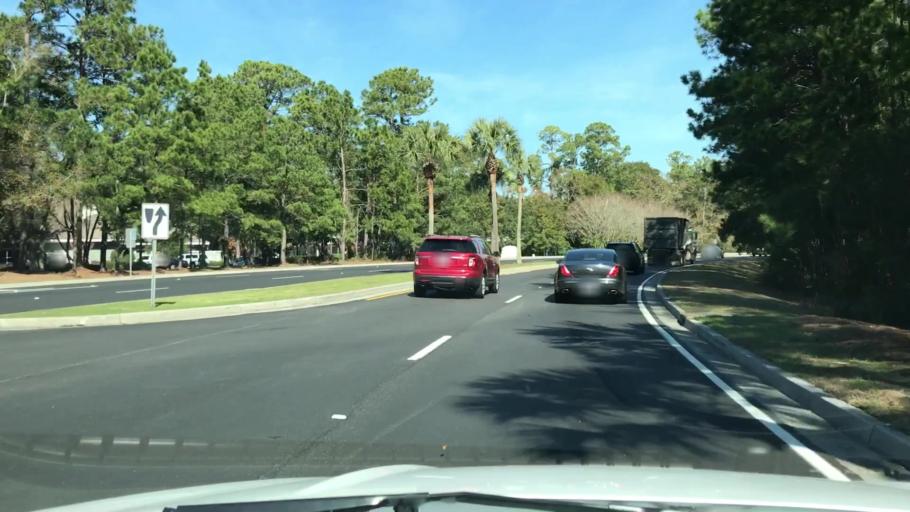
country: US
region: South Carolina
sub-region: Beaufort County
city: Hilton Head Island
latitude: 32.2193
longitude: -80.7122
